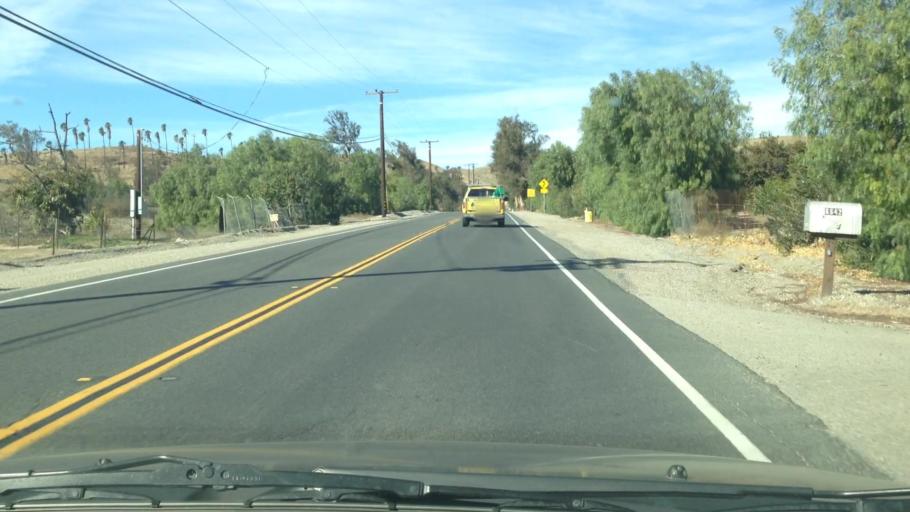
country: US
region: California
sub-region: Ventura County
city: Moorpark
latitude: 34.3251
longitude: -118.9024
